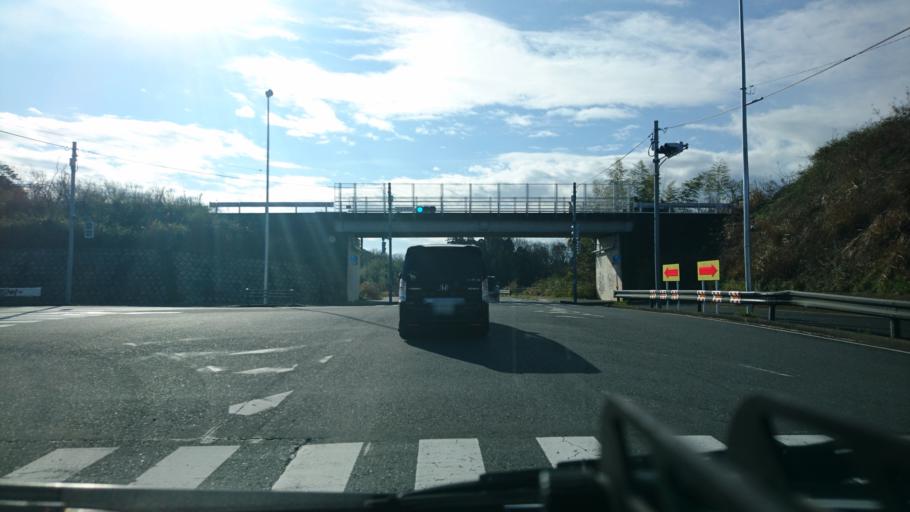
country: JP
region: Chiba
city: Kisarazu
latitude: 35.3557
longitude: 139.9379
